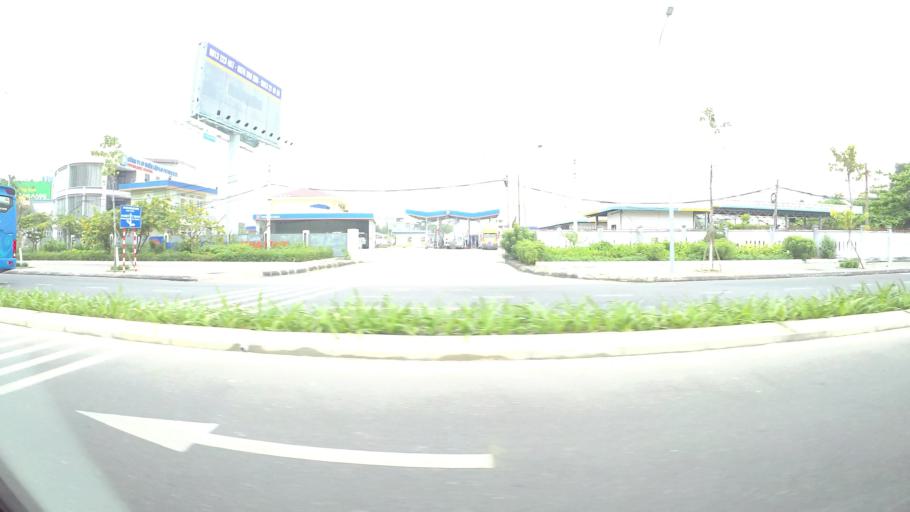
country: VN
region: Da Nang
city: Thanh Khe
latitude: 16.0577
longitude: 108.2041
